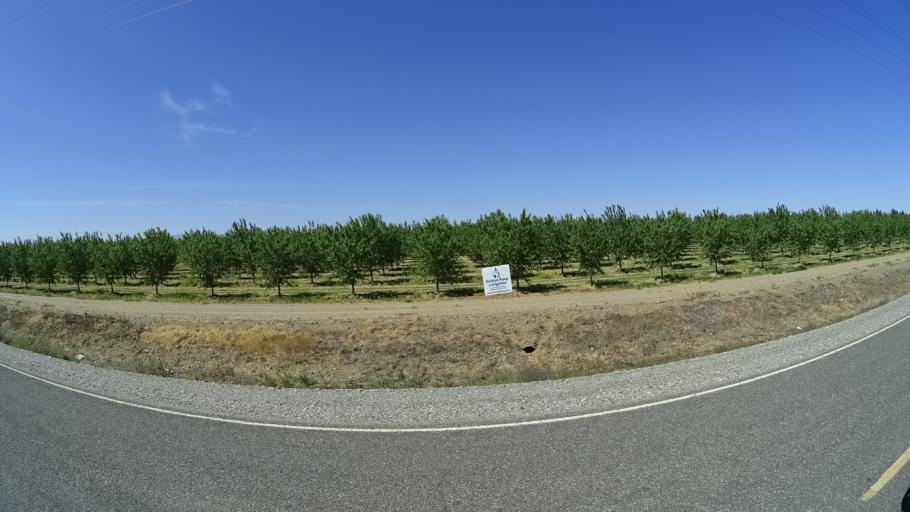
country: US
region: California
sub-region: Glenn County
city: Orland
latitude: 39.6880
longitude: -122.1780
